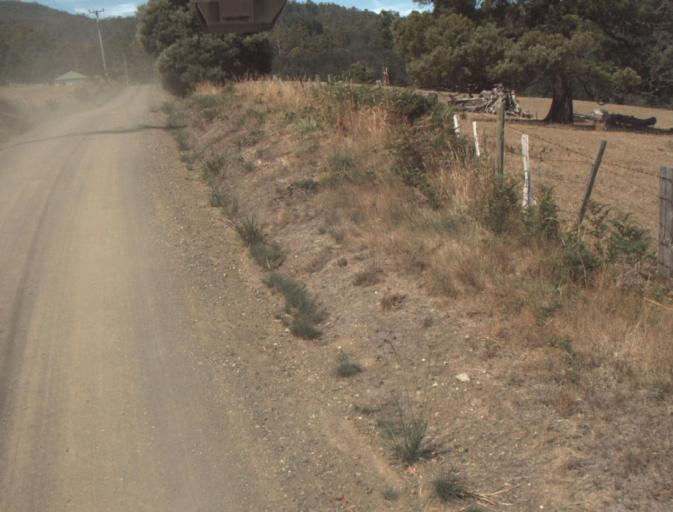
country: AU
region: Tasmania
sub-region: Launceston
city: Mayfield
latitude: -41.2524
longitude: 147.1850
